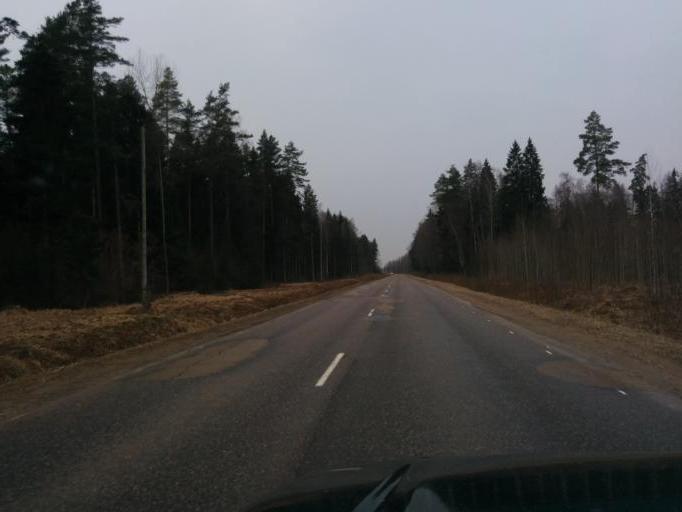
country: LV
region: Ikskile
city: Ikskile
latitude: 56.8116
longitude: 24.4816
